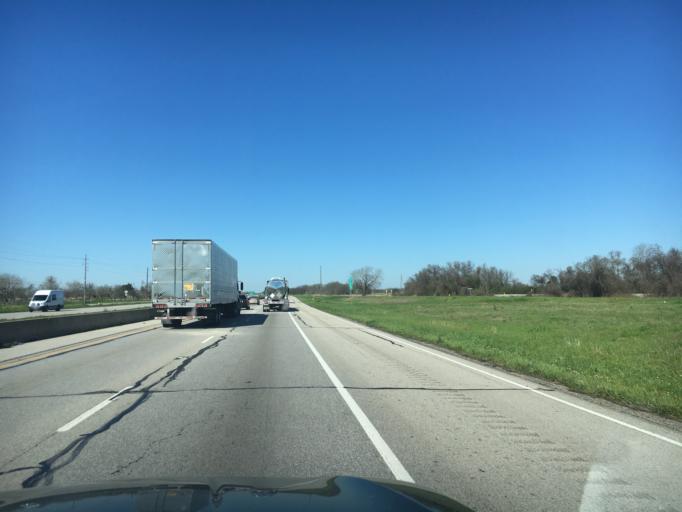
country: US
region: Texas
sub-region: Austin County
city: Sealy
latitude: 29.7738
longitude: -96.0792
